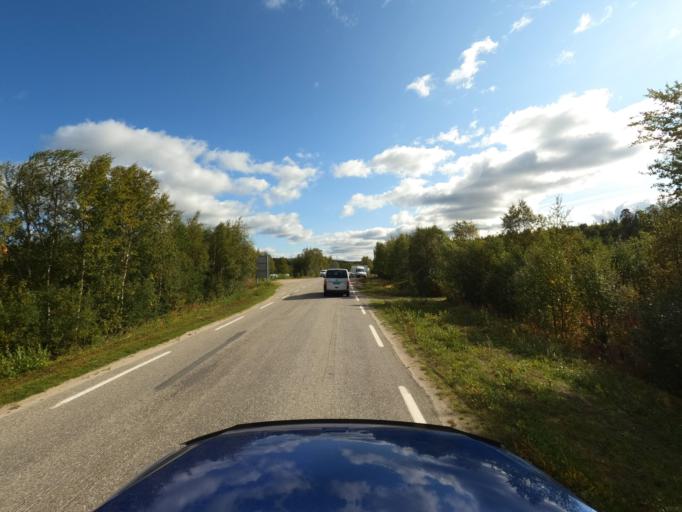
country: NO
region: Finnmark Fylke
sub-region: Karasjok
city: Karasjohka
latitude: 69.3998
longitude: 25.8303
